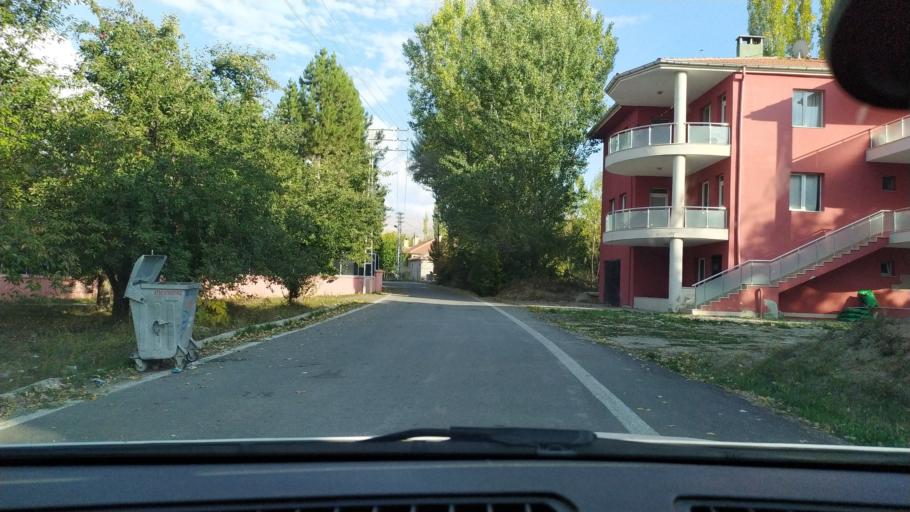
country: TR
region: Kayseri
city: Akkisla
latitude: 39.0005
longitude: 36.1708
